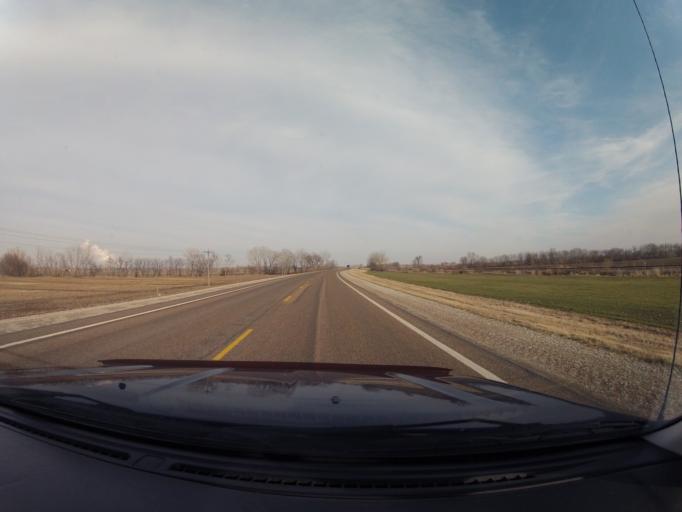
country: US
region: Kansas
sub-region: Pottawatomie County
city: Wamego
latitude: 39.2167
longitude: -96.2177
